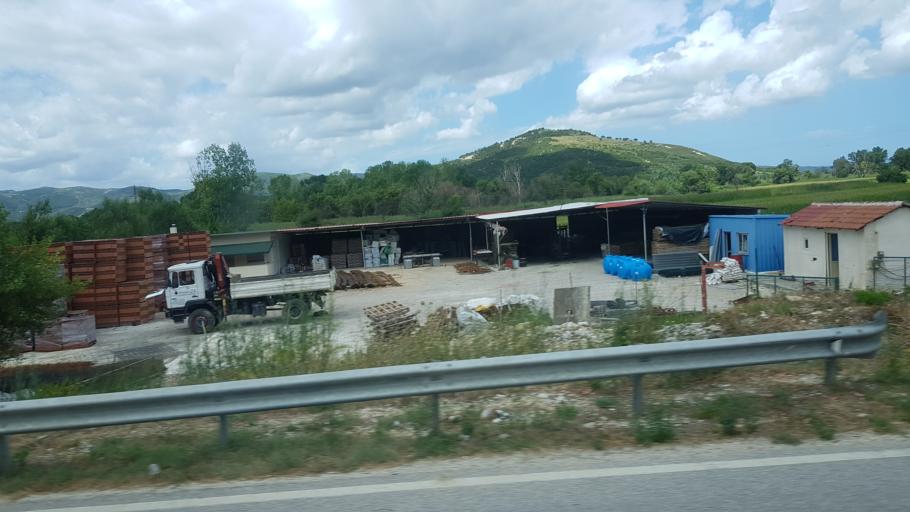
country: AL
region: Fier
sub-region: Rrethi i Mallakastres
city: Hekal
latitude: 40.5170
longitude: 19.7419
